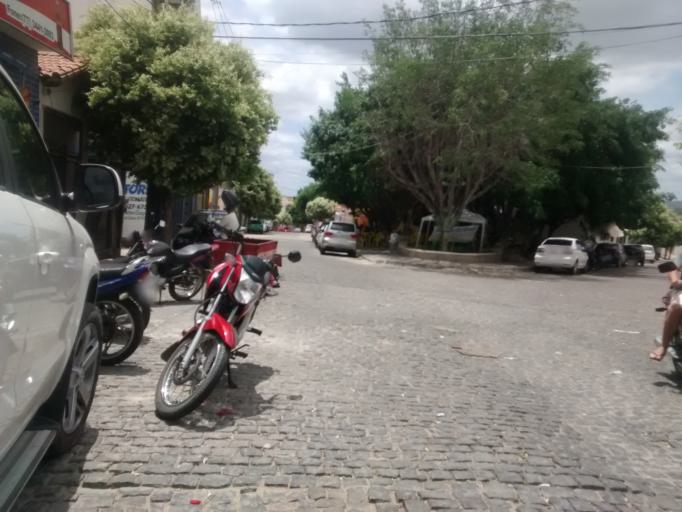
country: BR
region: Bahia
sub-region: Brumado
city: Brumado
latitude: -14.2106
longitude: -41.6752
